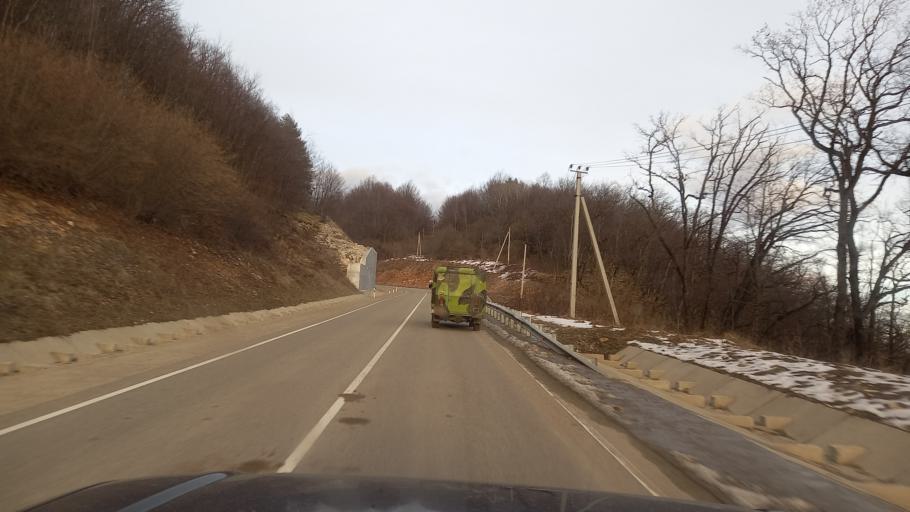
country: RU
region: Adygeya
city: Kamennomostskiy
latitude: 44.2182
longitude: 39.9766
